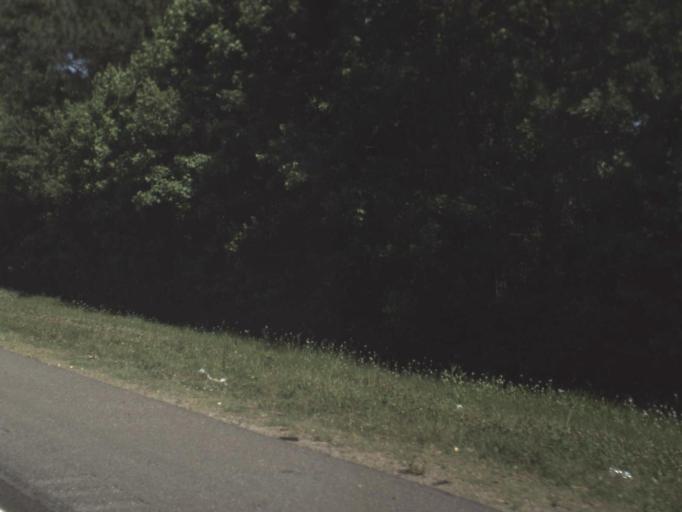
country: US
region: Florida
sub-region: Duval County
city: Baldwin
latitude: 30.3106
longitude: -81.8293
